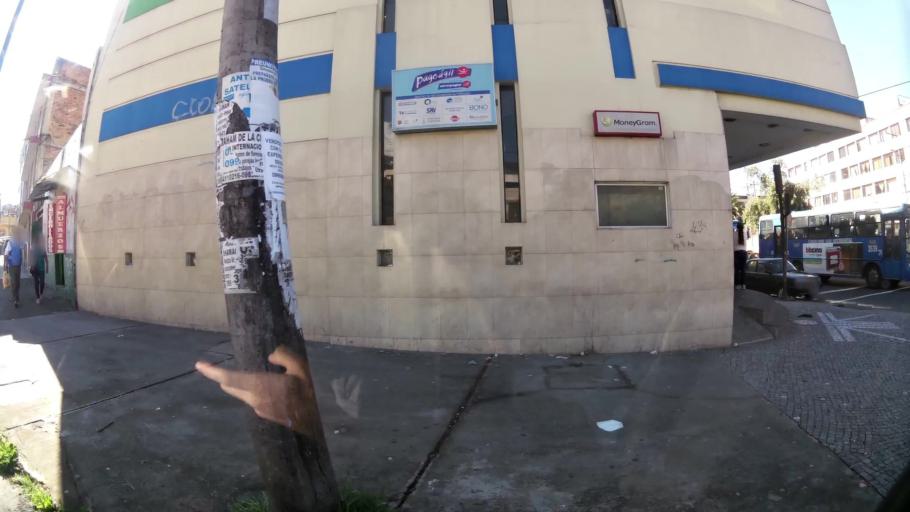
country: EC
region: Pichincha
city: Quito
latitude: -0.2416
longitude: -78.5321
